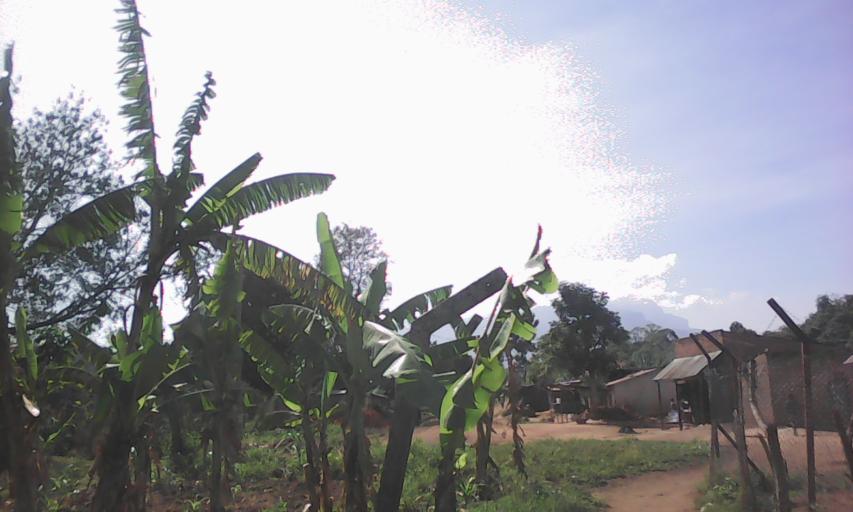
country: UG
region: Eastern Region
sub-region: Mbale District
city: Mbale
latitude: 1.0756
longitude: 34.1548
